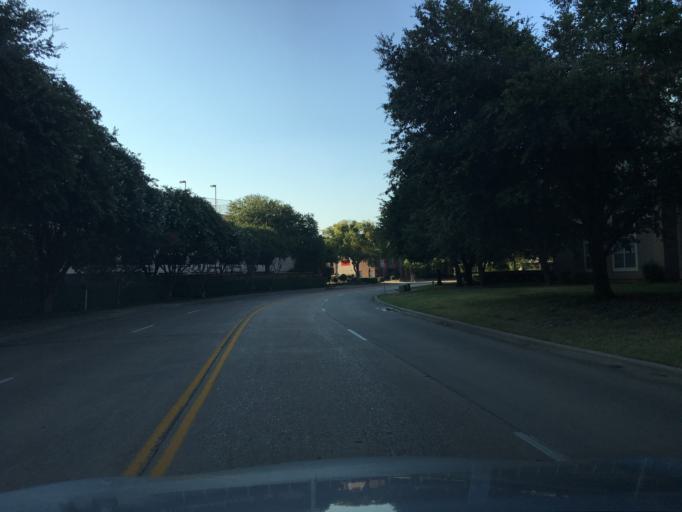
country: US
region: Texas
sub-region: Dallas County
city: Addison
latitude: 32.9676
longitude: -96.8196
